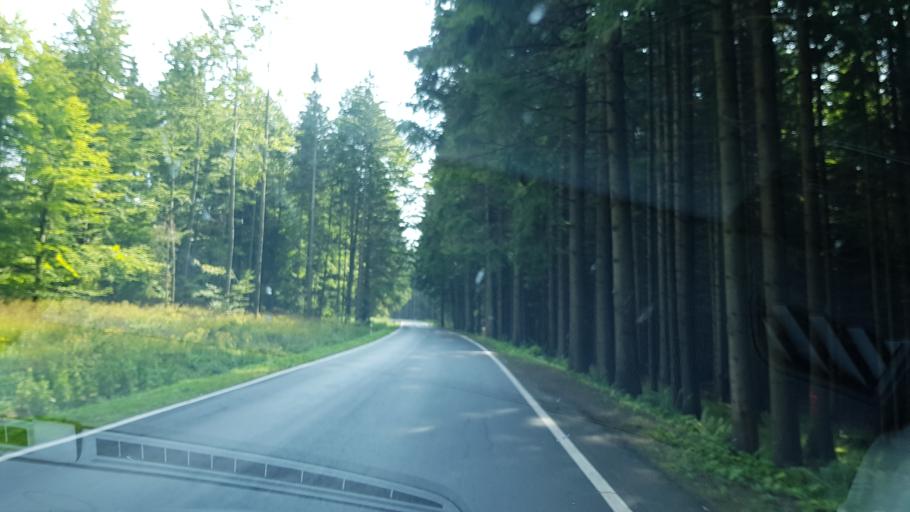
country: CZ
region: Olomoucky
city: Ceska Ves
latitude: 50.2184
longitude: 17.2675
